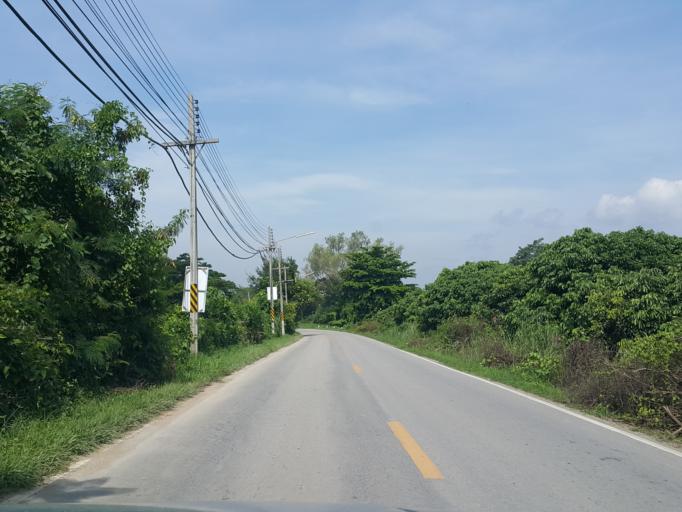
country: TH
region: Chiang Mai
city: Saraphi
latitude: 18.6908
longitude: 99.0578
